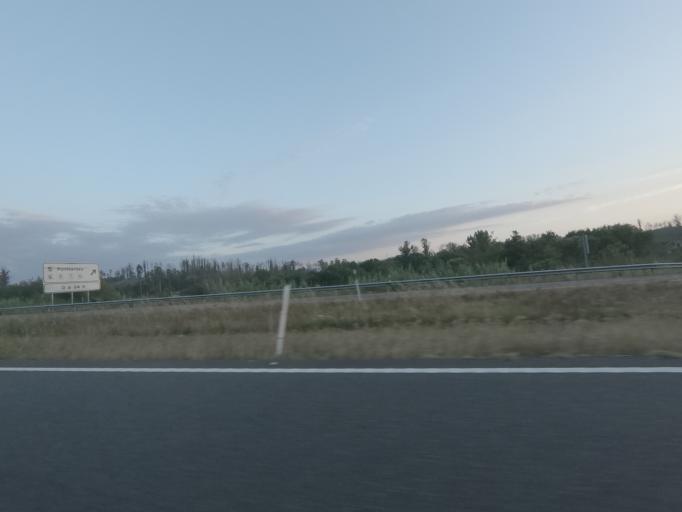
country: ES
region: Galicia
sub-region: Provincia de Pontevedra
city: Ponteareas
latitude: 42.1529
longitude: -8.4811
